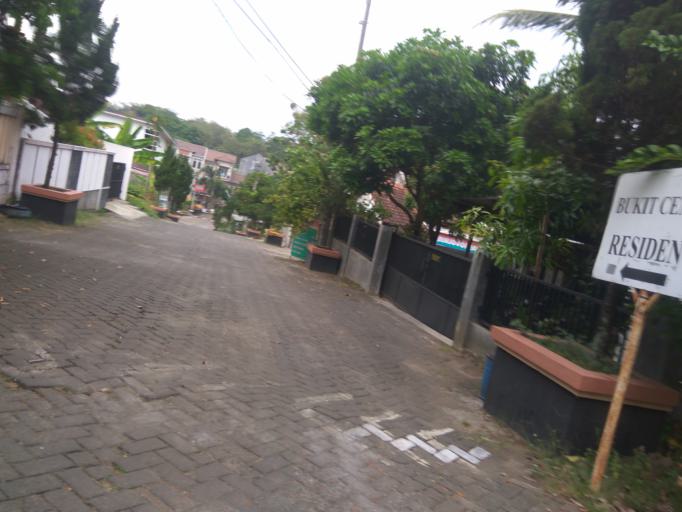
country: ID
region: Central Java
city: Semarang
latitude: -7.0655
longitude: 110.4472
